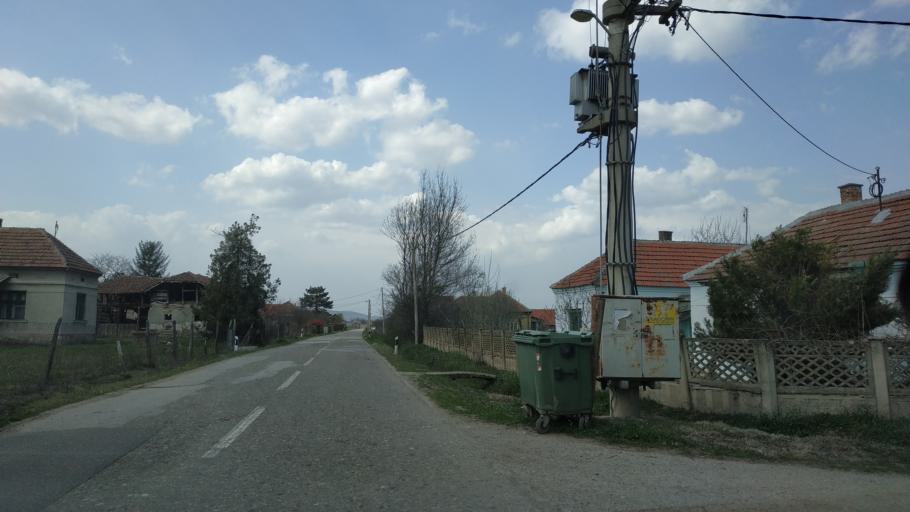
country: RS
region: Central Serbia
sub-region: Nisavski Okrug
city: Aleksinac
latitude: 43.5585
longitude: 21.6067
